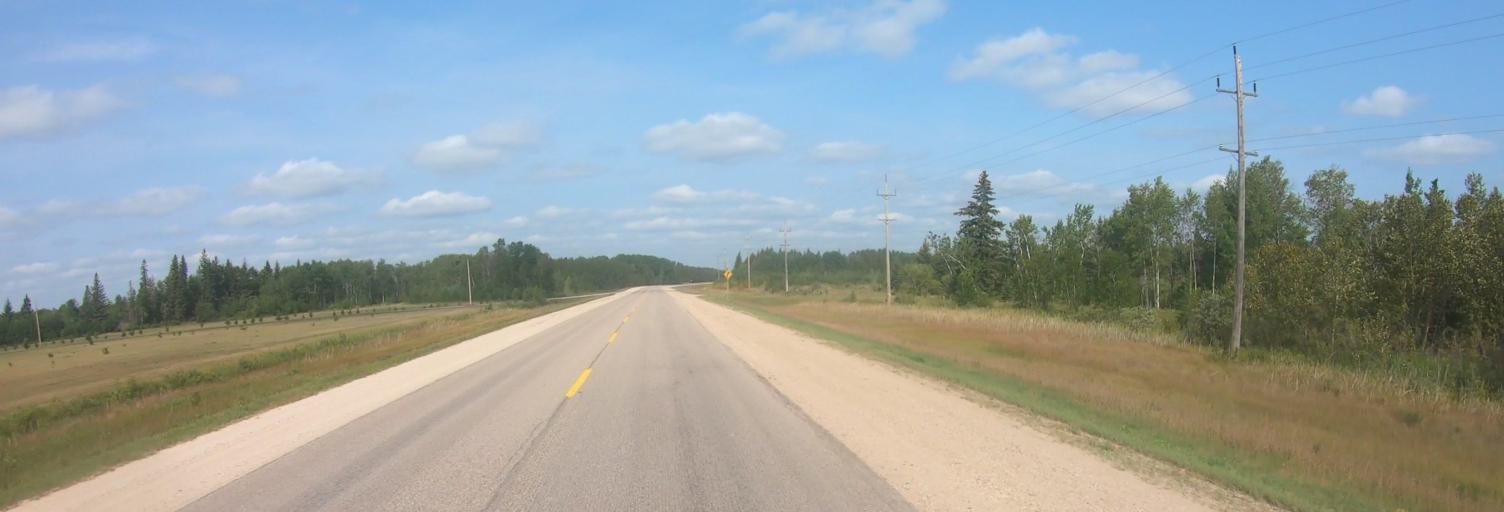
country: CA
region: Manitoba
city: La Broquerie
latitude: 49.1854
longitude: -96.2462
